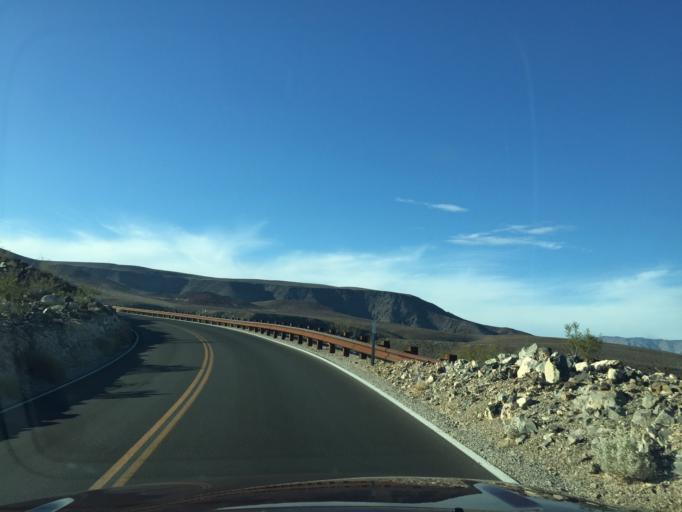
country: US
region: California
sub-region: San Bernardino County
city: Searles Valley
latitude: 36.3445
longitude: -117.5178
